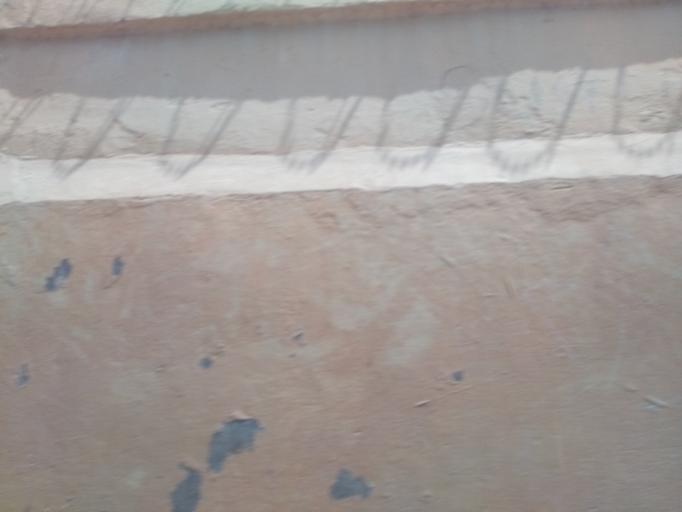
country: TZ
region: Dar es Salaam
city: Magomeni
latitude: -6.7732
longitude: 39.2743
